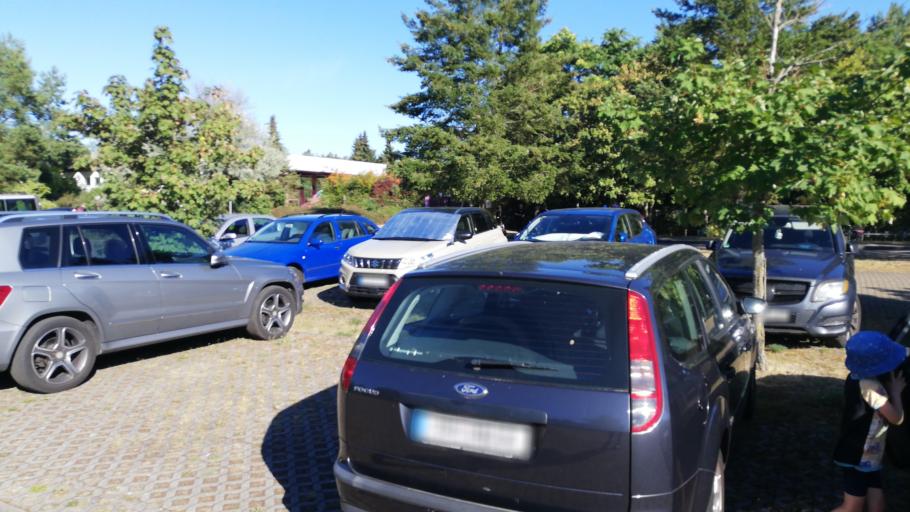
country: DE
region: Brandenburg
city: Premnitz
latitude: 52.5394
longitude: 12.3523
